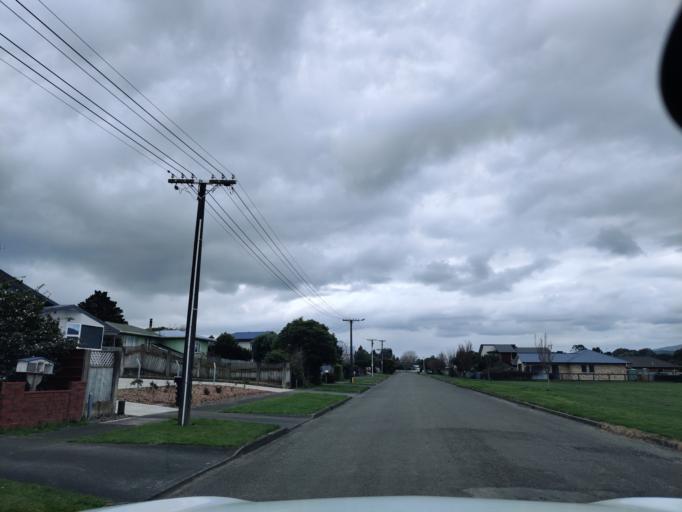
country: NZ
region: Manawatu-Wanganui
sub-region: Palmerston North City
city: Palmerston North
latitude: -40.2921
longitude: 175.7593
